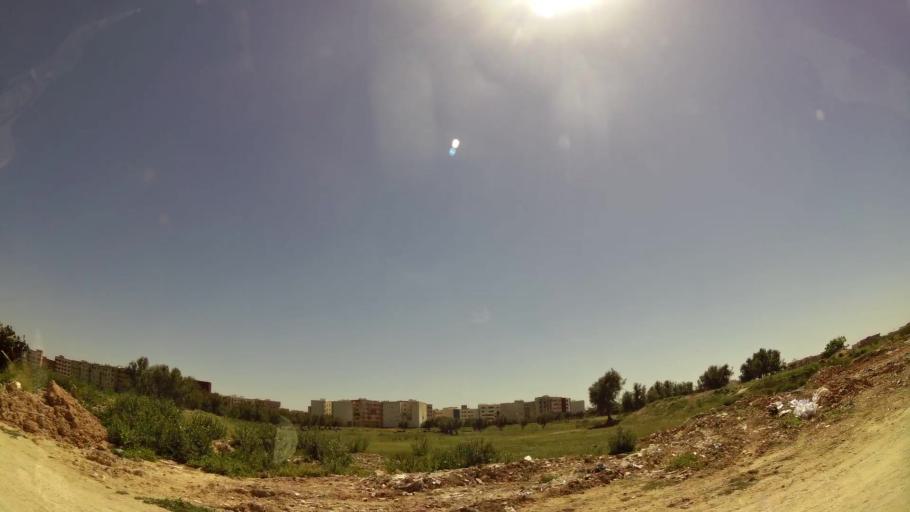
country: MA
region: Meknes-Tafilalet
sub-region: Meknes
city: Meknes
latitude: 33.8630
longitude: -5.5544
